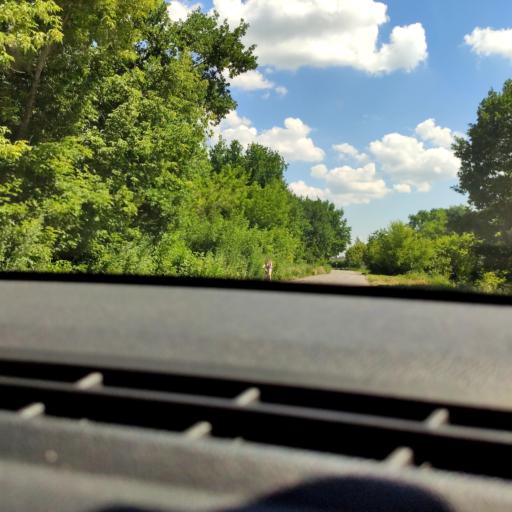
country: RU
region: Samara
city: Podstepki
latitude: 53.5758
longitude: 49.0570
